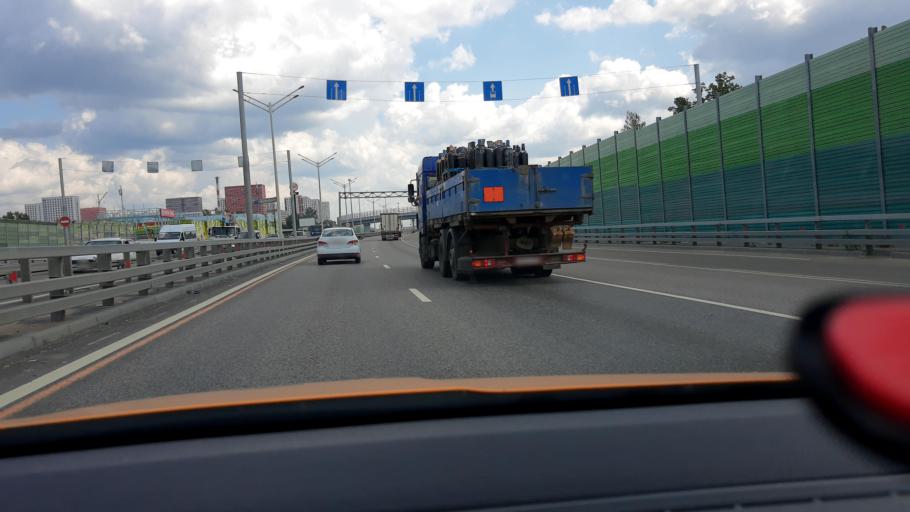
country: RU
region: Moskovskaya
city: Odintsovo
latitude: 55.6488
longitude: 37.2521
